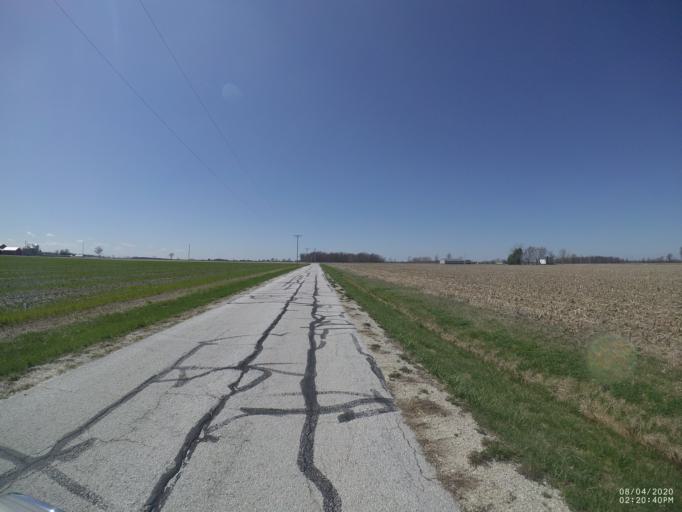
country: US
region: Ohio
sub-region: Sandusky County
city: Gibsonburg
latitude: 41.2894
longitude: -83.2574
